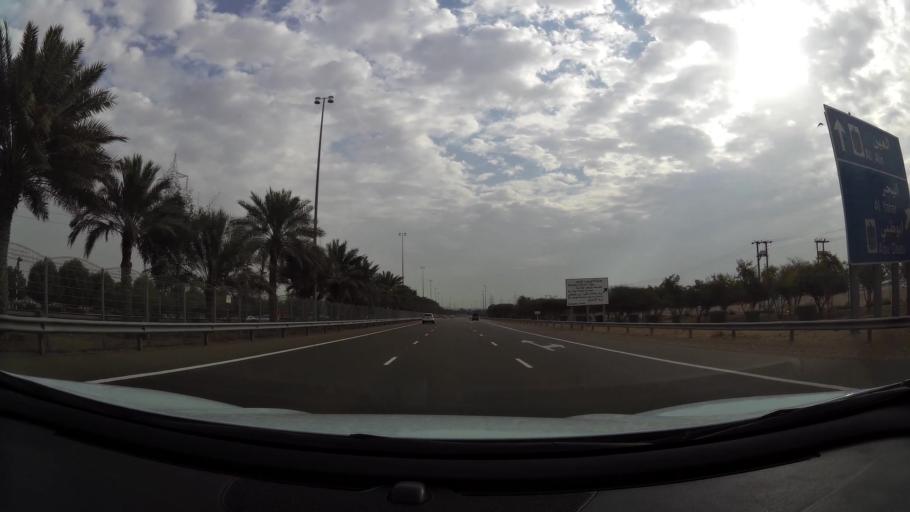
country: AE
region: Abu Dhabi
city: Al Ain
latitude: 24.2229
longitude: 55.5546
